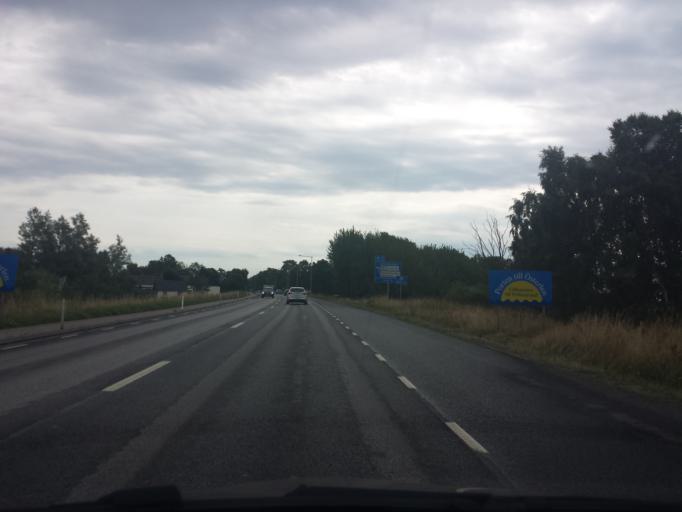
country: SE
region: Skane
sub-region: Ystads Kommun
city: Kopingebro
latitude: 55.4355
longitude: 13.9222
